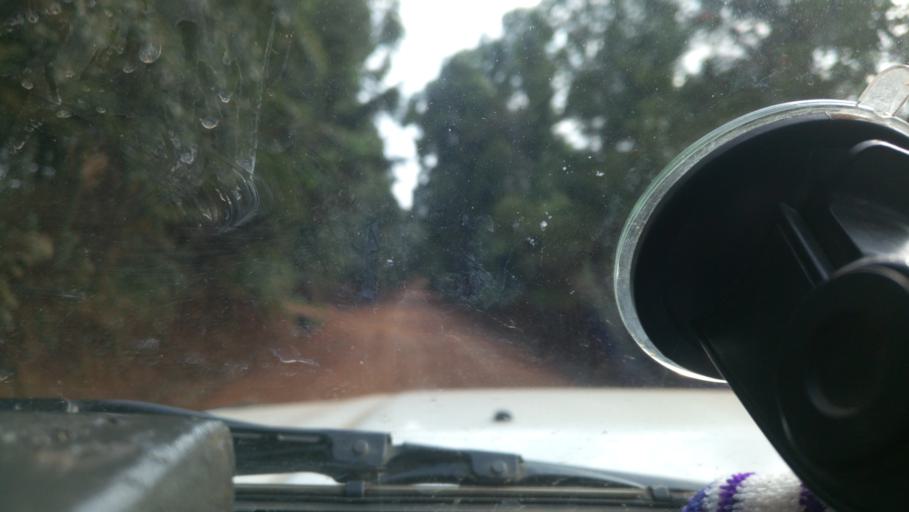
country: KE
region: Kericho
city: Litein
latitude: -0.5560
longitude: 35.1979
